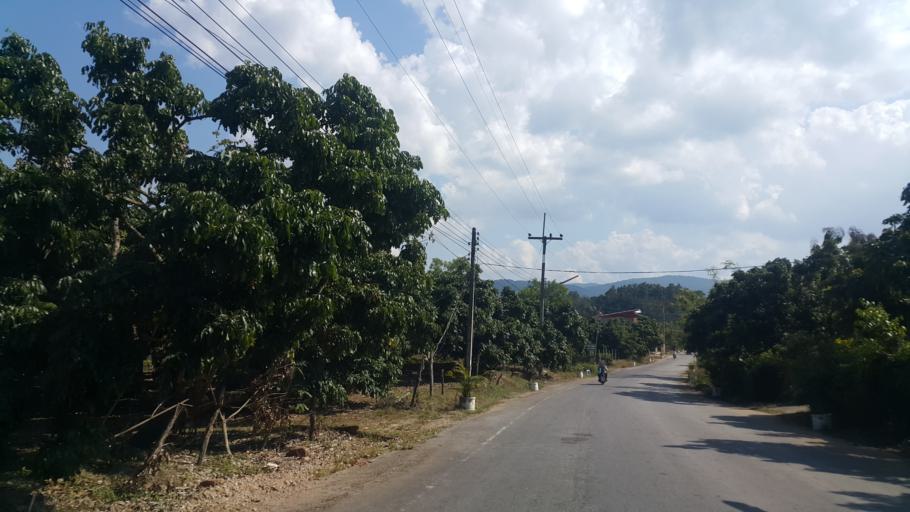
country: TH
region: Lamphun
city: Ban Thi
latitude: 18.6236
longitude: 99.1586
